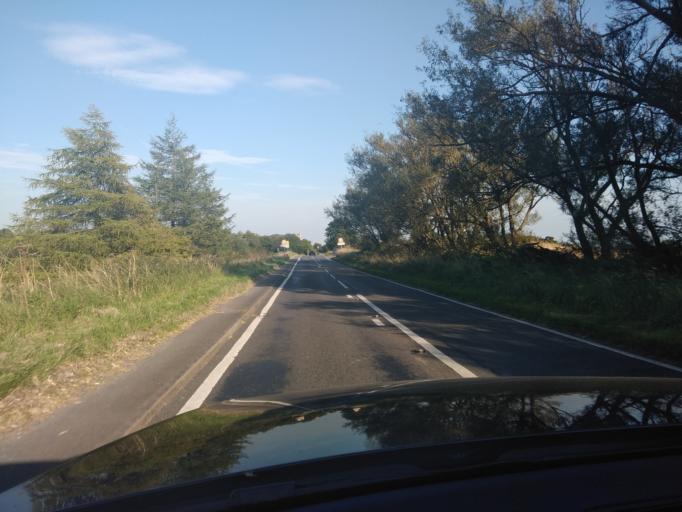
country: GB
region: England
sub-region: Derbyshire
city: Dronfield
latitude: 53.2954
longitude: -1.5292
